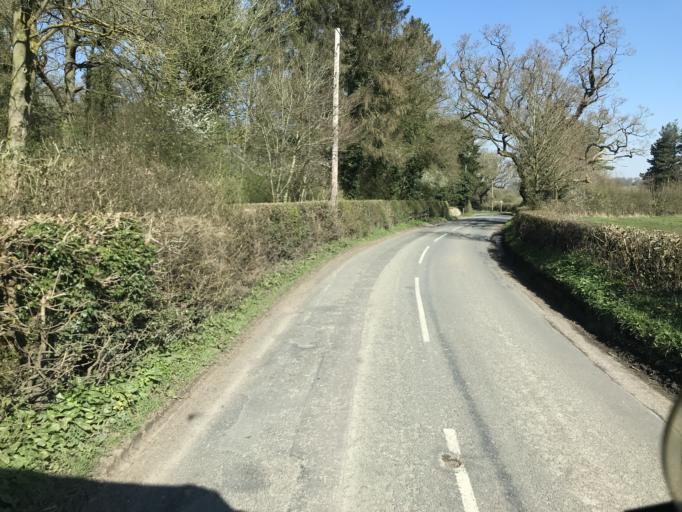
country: GB
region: England
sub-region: Cheshire West and Chester
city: Aldford
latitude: 53.1419
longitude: -2.8424
